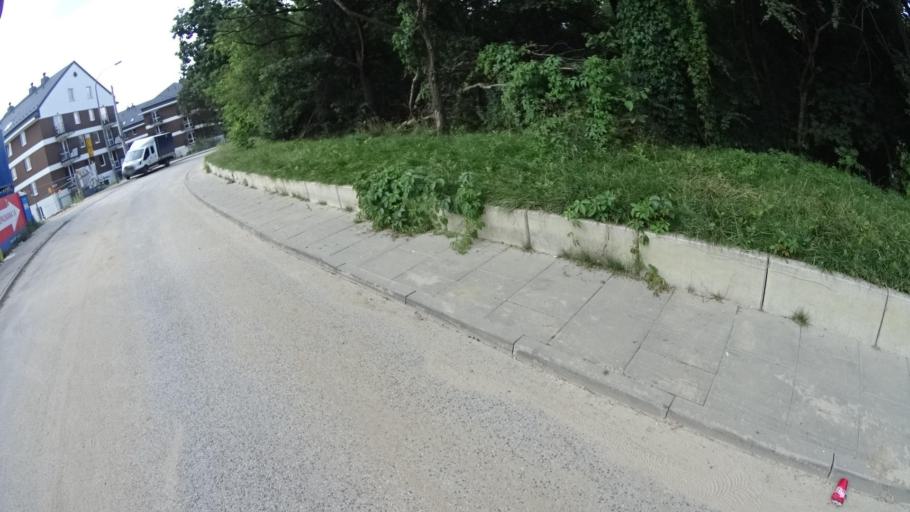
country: PL
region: Masovian Voivodeship
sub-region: Warszawa
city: Ursus
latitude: 52.2197
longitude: 20.8901
